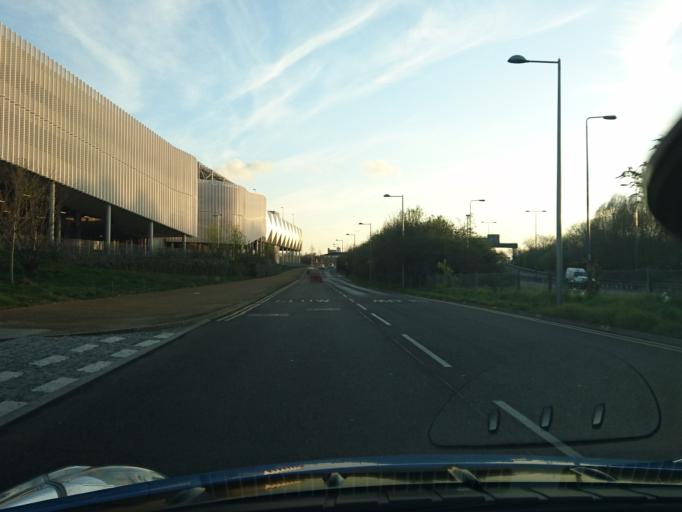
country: GB
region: England
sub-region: Greater London
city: Hackney
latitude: 51.5500
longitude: -0.0232
